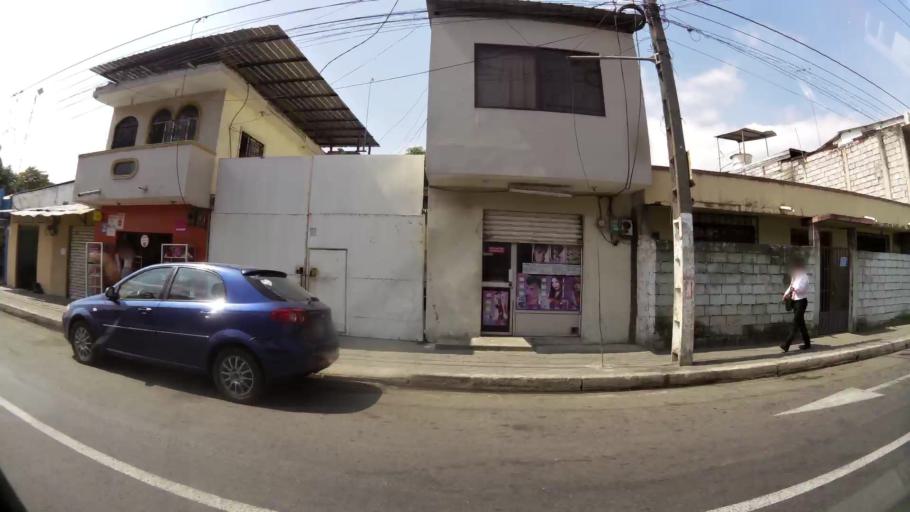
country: EC
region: Guayas
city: Eloy Alfaro
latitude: -2.1564
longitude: -79.8374
